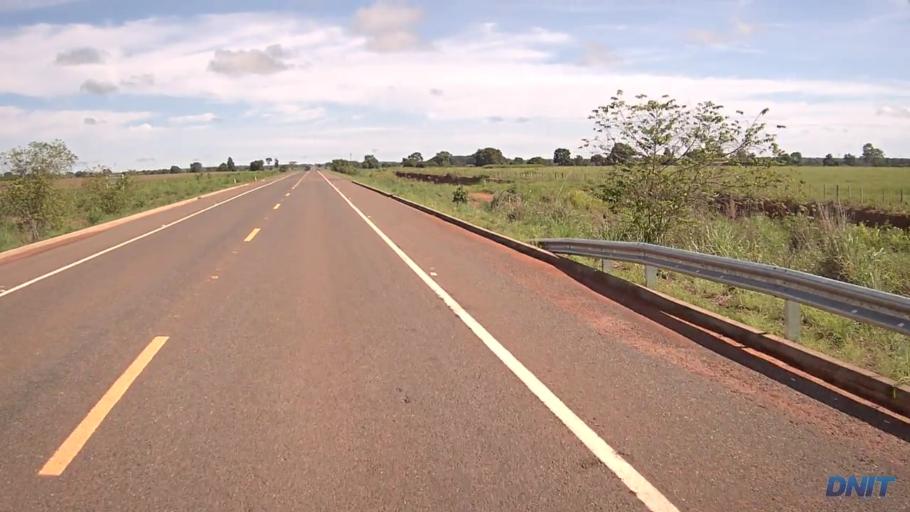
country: BR
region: Goias
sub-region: Sao Miguel Do Araguaia
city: Sao Miguel do Araguaia
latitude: -13.3938
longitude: -50.1370
